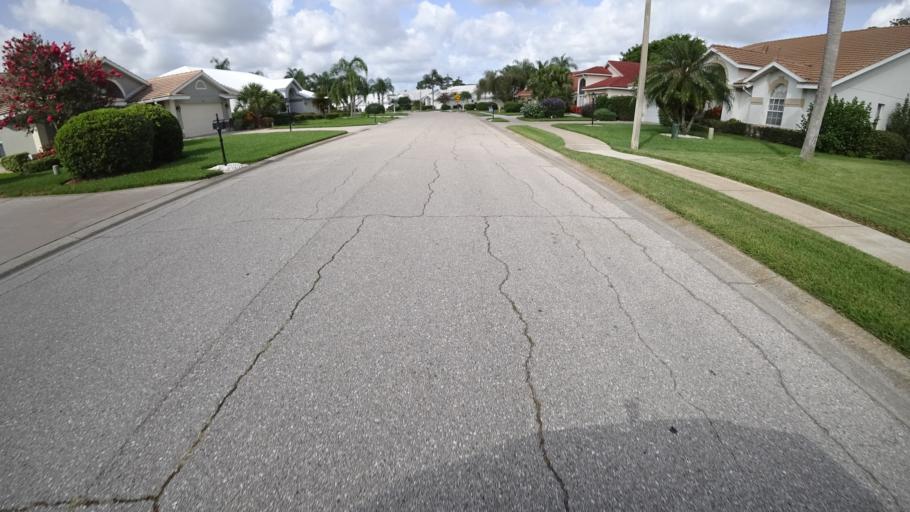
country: US
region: Florida
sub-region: Manatee County
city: Samoset
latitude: 27.4407
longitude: -82.4798
